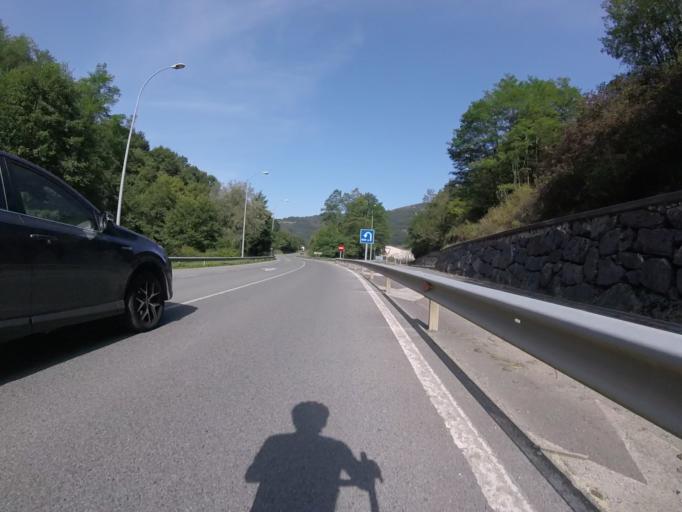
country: ES
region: Navarre
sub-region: Provincia de Navarra
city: Doneztebe
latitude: 43.1371
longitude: -1.5556
